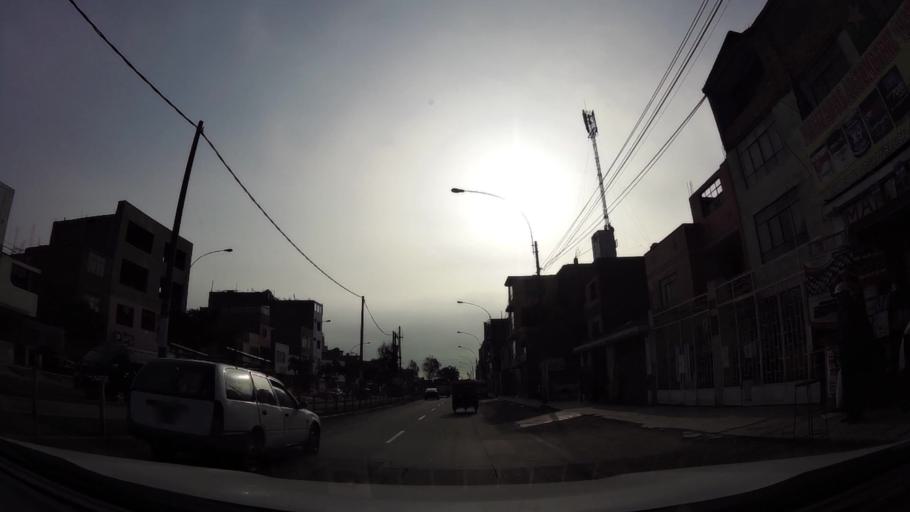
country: PE
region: Lima
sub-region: Lima
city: Independencia
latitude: -12.0249
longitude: -77.0784
